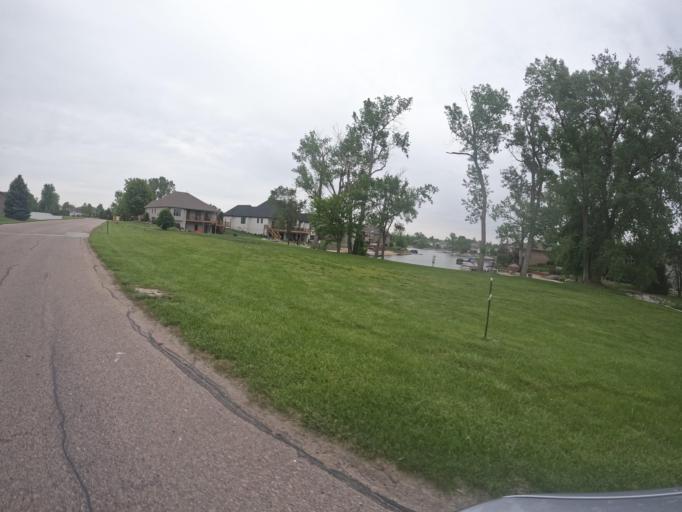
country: US
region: Nebraska
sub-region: Sarpy County
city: Offutt Air Force Base
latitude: 41.0481
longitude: -95.9562
